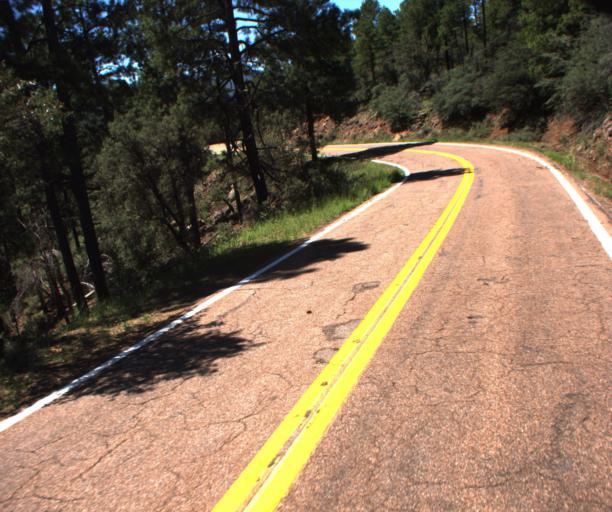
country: US
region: Arizona
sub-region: Greenlee County
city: Morenci
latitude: 33.5144
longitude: -109.3186
